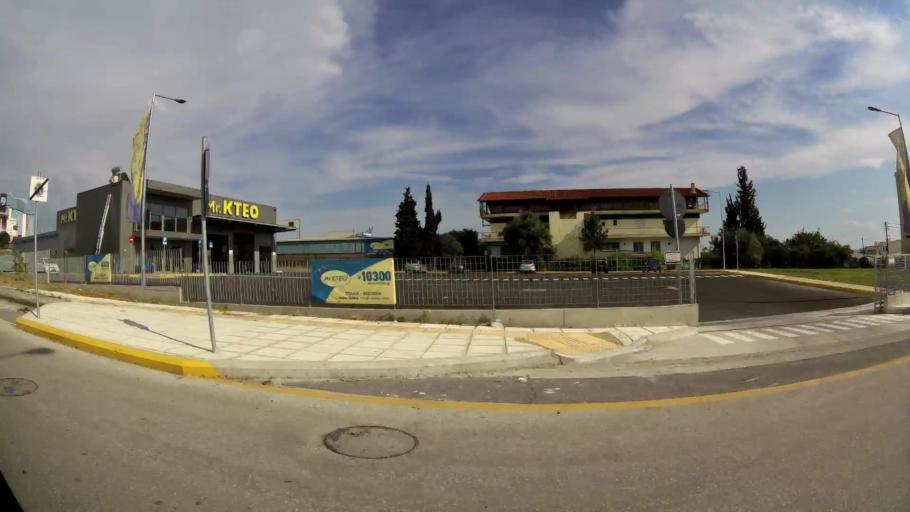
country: GR
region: Central Macedonia
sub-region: Nomos Thessalonikis
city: Kalamaria
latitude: 40.5654
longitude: 22.9783
